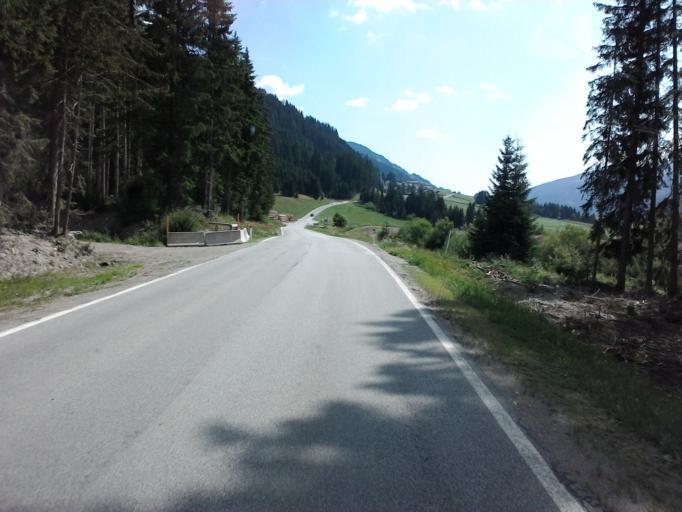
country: AT
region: Tyrol
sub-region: Politischer Bezirk Lienz
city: Obertilliach
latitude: 46.7100
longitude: 12.5894
